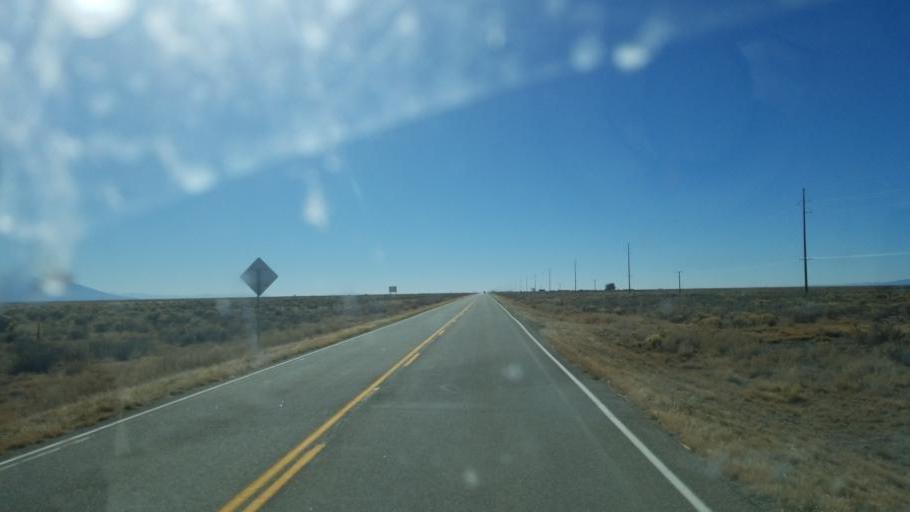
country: US
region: Colorado
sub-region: Saguache County
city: Saguache
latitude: 37.9902
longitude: -105.9075
